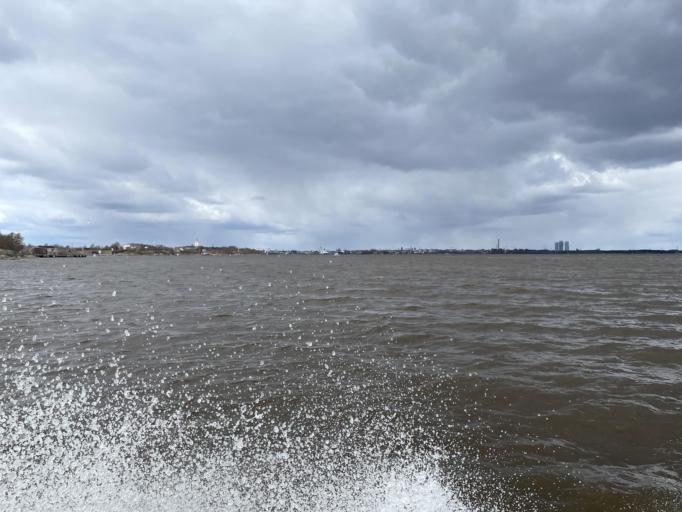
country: FI
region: Uusimaa
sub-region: Helsinki
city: Helsinki
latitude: 60.1393
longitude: 25.0139
